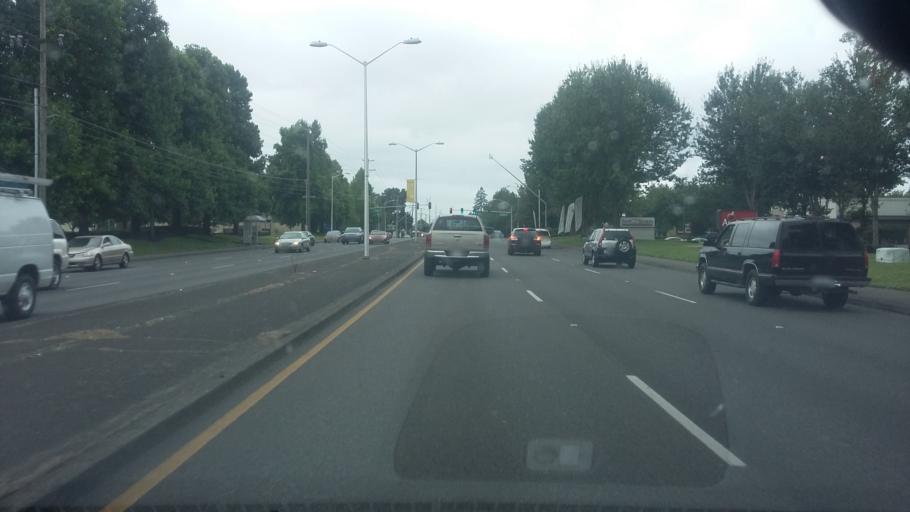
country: US
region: Washington
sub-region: Clark County
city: Orchards
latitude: 45.6195
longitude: -122.5405
